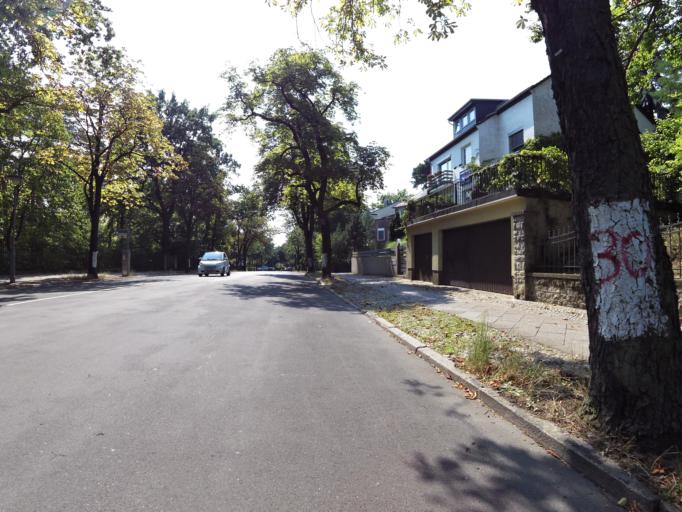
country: DE
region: Berlin
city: Steglitz Bezirk
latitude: 52.4566
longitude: 13.3131
